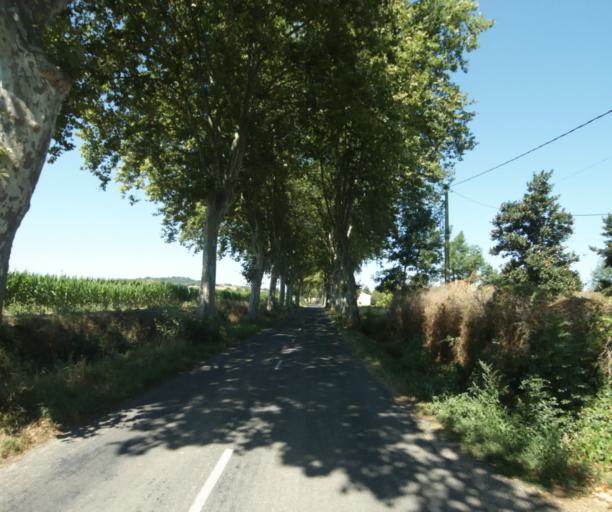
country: FR
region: Midi-Pyrenees
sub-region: Departement de la Haute-Garonne
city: Revel
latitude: 43.4987
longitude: 1.9595
